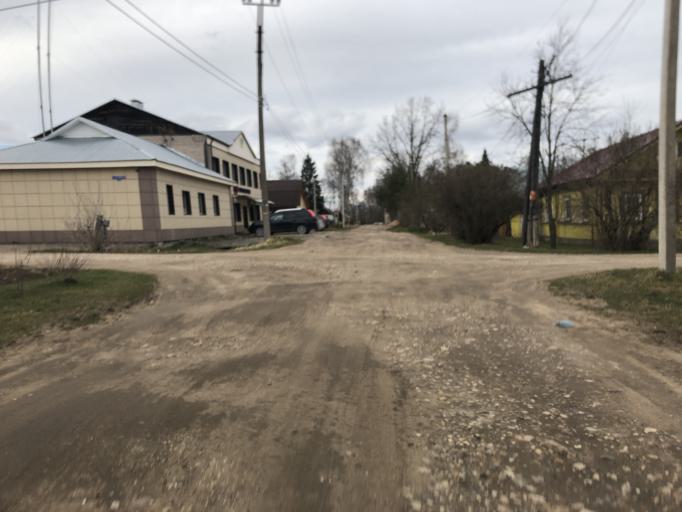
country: RU
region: Tverskaya
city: Rzhev
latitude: 56.2540
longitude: 34.3174
